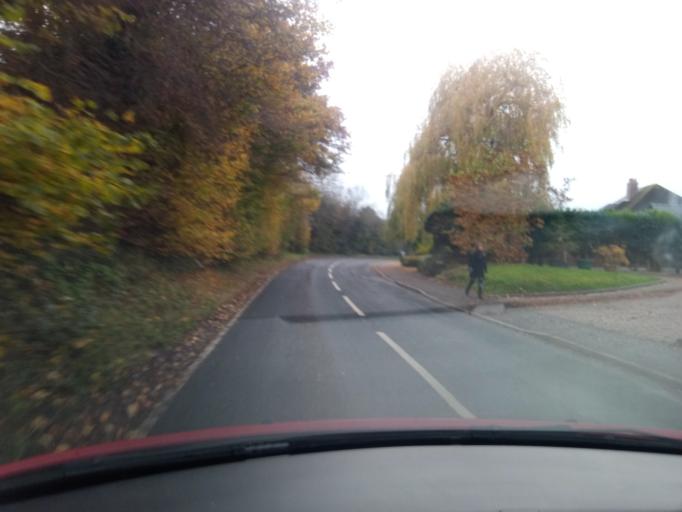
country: GB
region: England
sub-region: Derbyshire
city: Little Eaton
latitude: 52.9367
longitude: -1.4236
